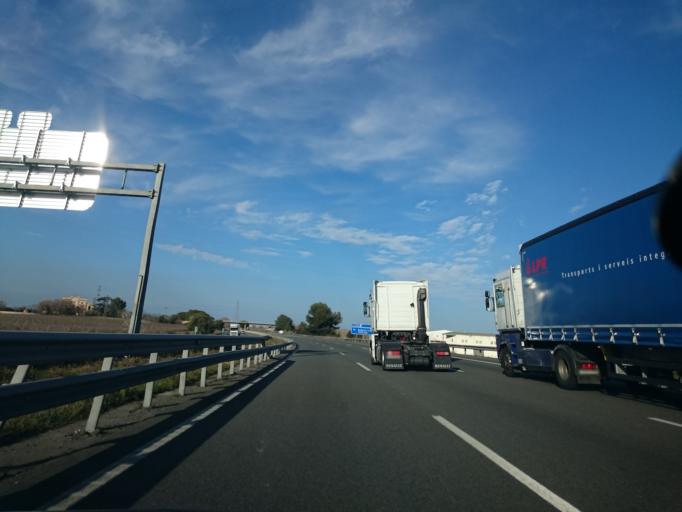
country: ES
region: Catalonia
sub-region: Provincia de Barcelona
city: Vilafranca del Penedes
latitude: 41.3550
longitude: 1.7227
